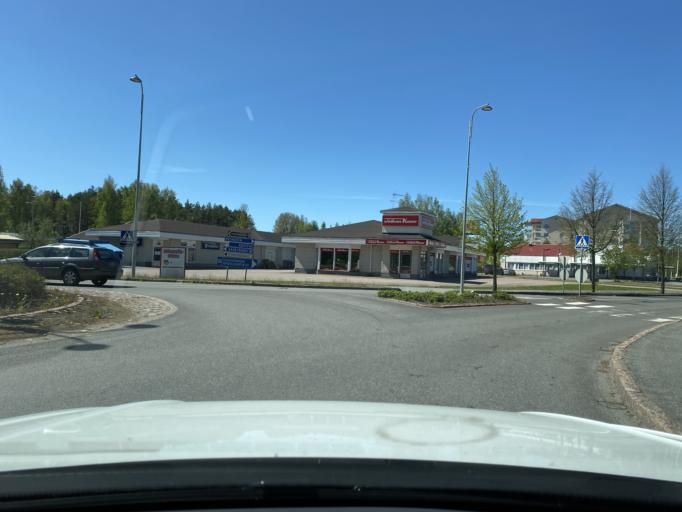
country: FI
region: Satakunta
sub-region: Rauma
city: Eura
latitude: 61.1299
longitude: 22.1437
